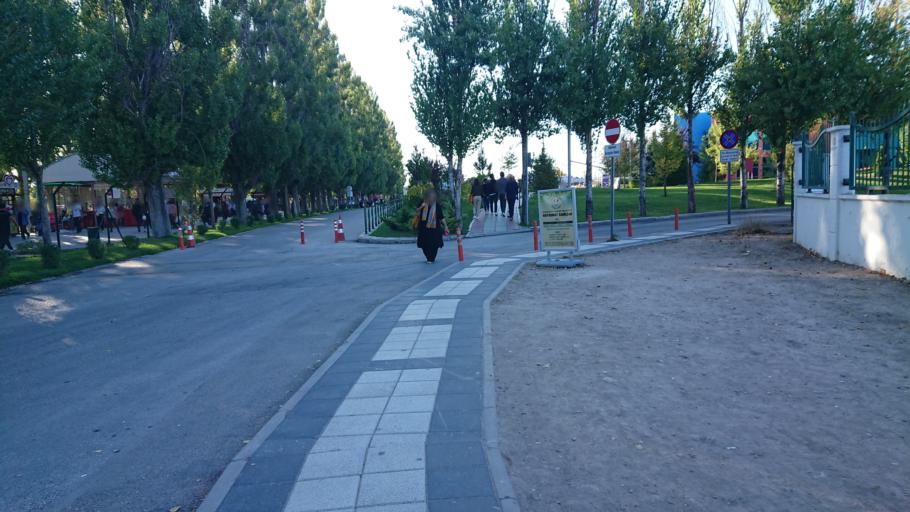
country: TR
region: Eskisehir
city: Eskisehir
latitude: 39.7648
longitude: 30.4740
